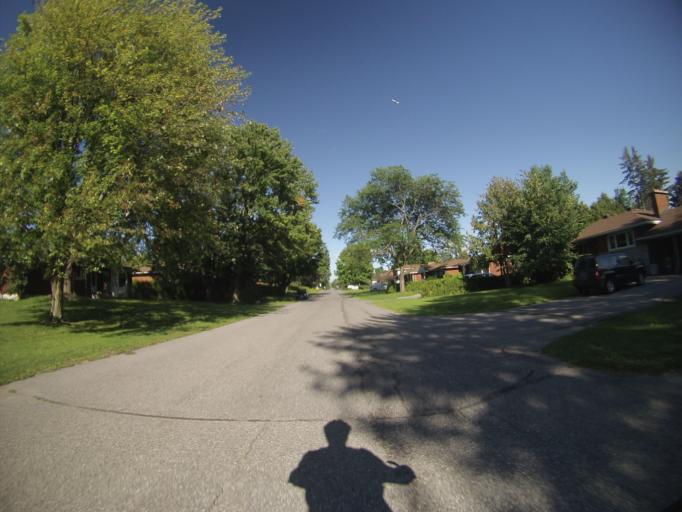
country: CA
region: Ontario
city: Ottawa
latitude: 45.3473
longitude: -75.7474
